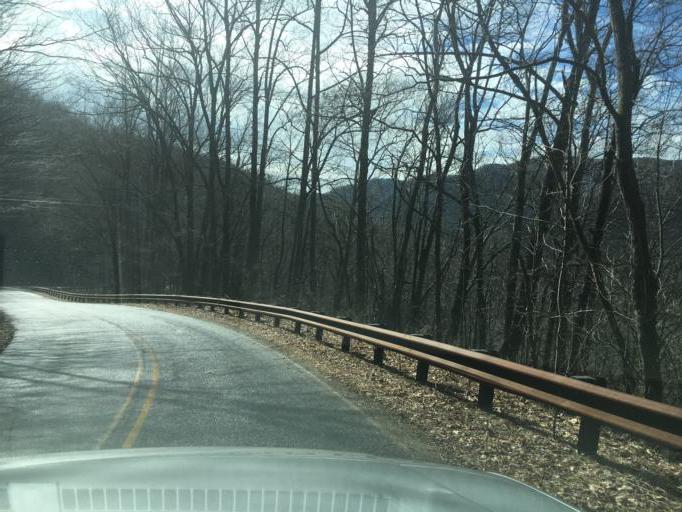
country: US
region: North Carolina
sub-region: Transylvania County
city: Brevard
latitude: 35.3712
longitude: -82.8107
